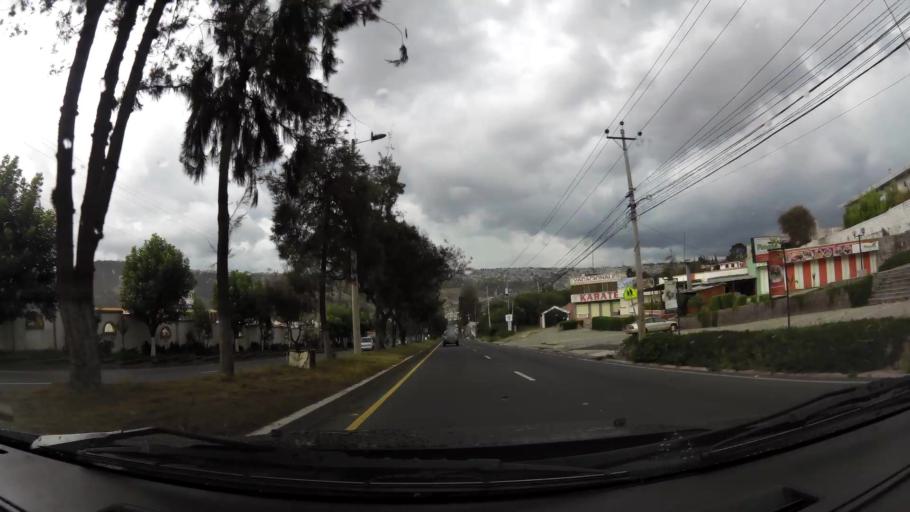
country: EC
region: Pichincha
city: Quito
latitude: -0.0659
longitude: -78.4619
